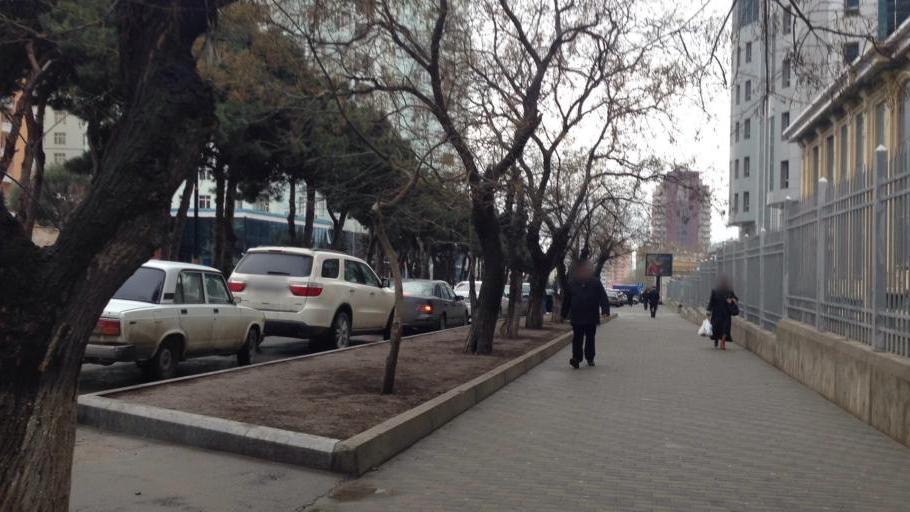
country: AZ
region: Baki
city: Baku
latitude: 40.3831
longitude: 49.8380
